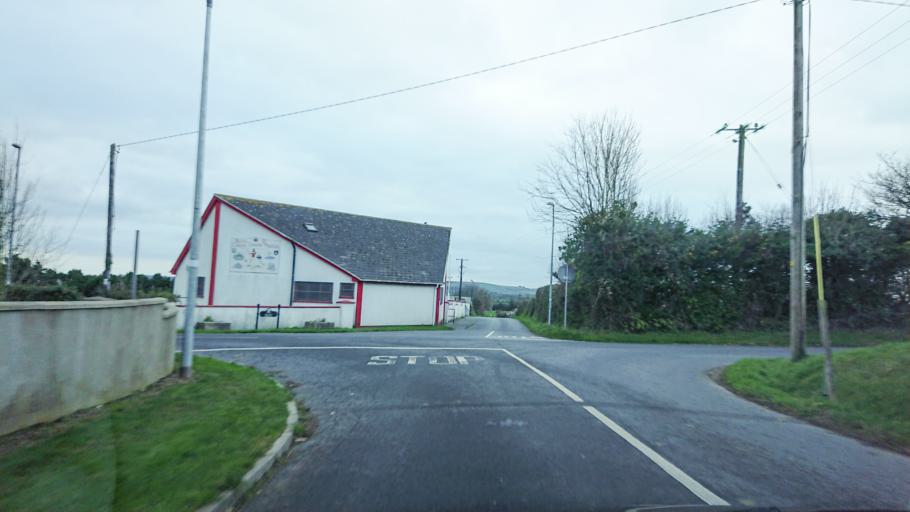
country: IE
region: Munster
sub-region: Waterford
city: Dunmore East
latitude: 52.2294
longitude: -6.9786
